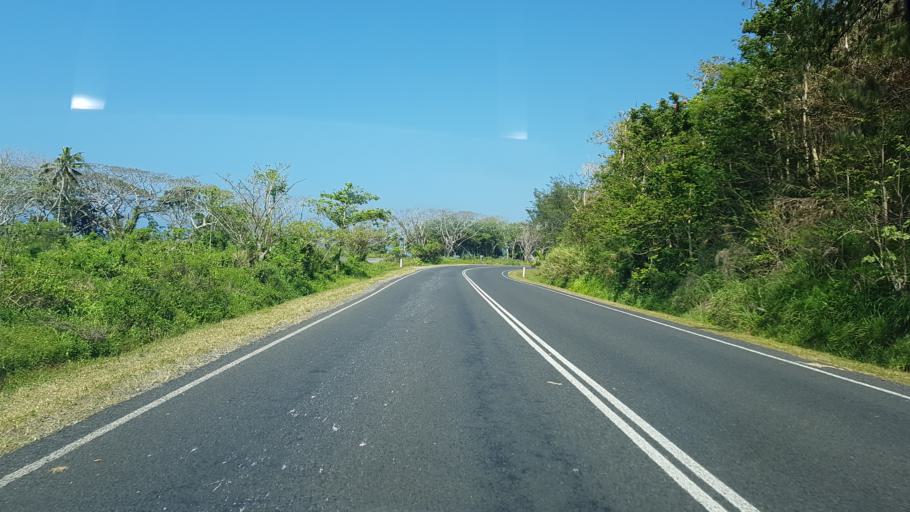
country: FJ
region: Western
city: Nadi
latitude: -18.1840
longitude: 177.6008
